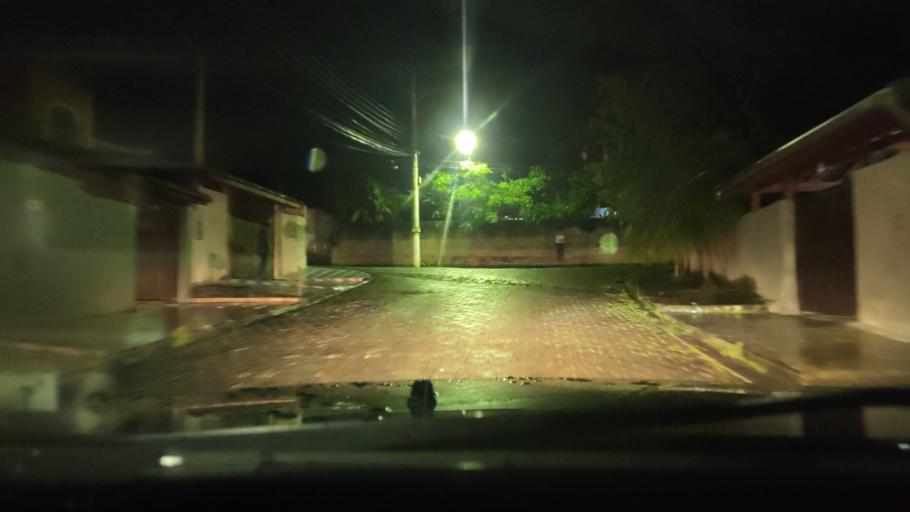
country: BR
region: Sao Paulo
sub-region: Sao Sebastiao
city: Sao Sebastiao
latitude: -23.7546
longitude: -45.4148
